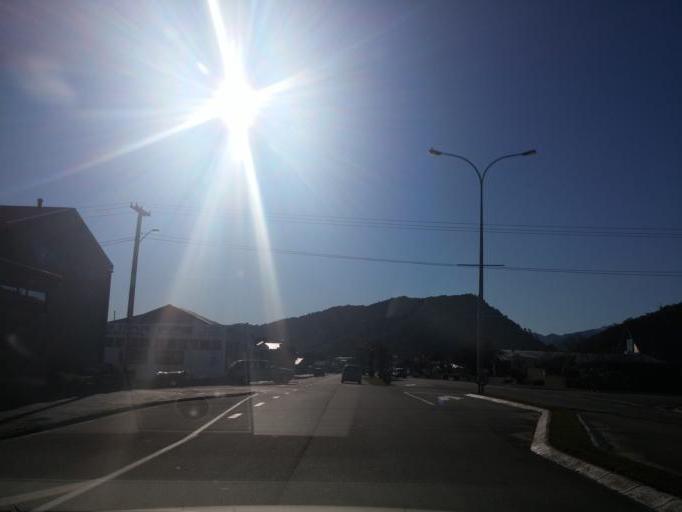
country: NZ
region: West Coast
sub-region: Grey District
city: Greymouth
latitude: -42.4546
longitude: 171.2080
